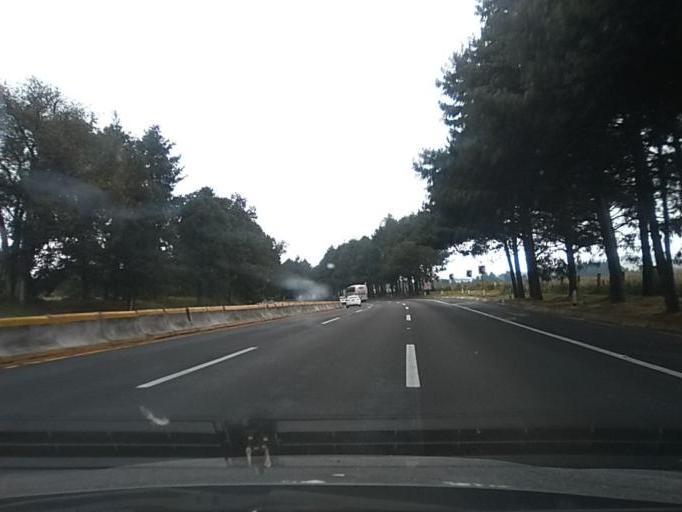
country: MX
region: Mexico City
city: Xochimilco
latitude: 19.1659
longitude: -99.1516
